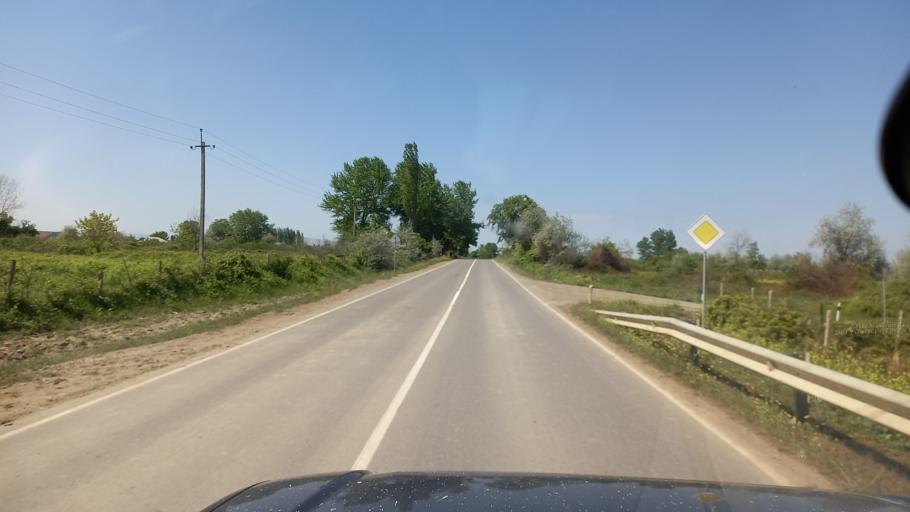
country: RU
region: Dagestan
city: Novaya Maka
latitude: 41.8124
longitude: 48.4047
